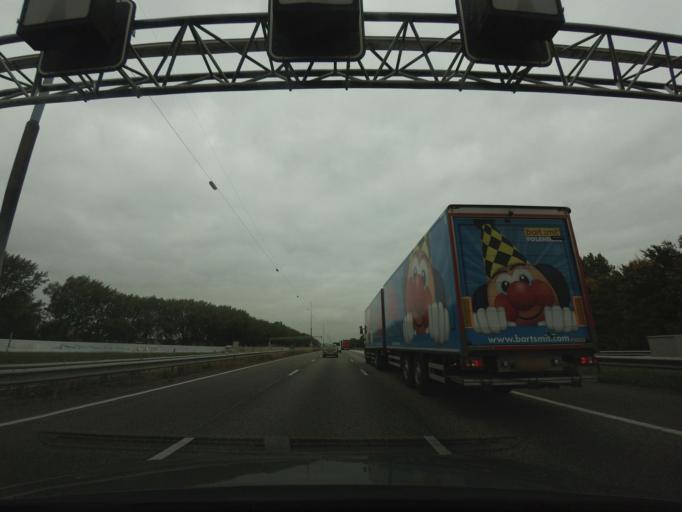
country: NL
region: North Holland
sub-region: Gemeente Diemen
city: Diemen
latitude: 52.3915
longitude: 4.9656
